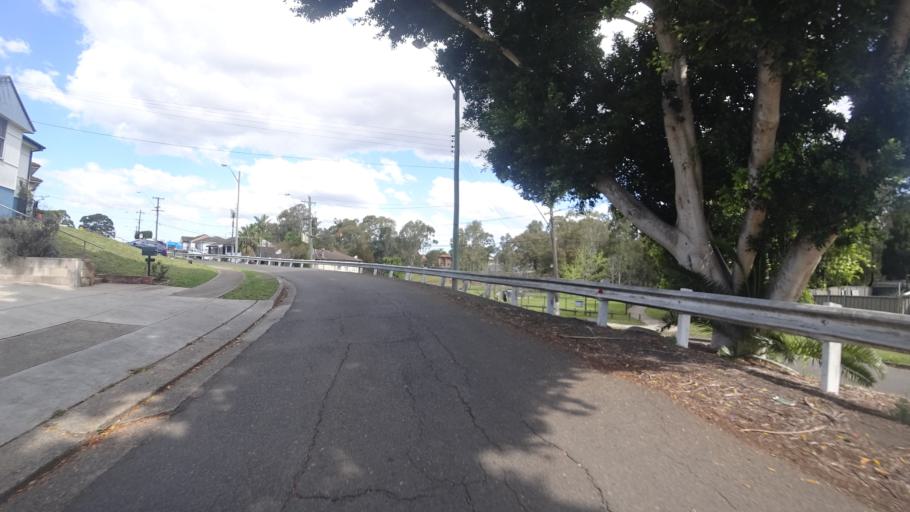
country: AU
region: New South Wales
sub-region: Fairfield
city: Cabramatta West
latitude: -33.9043
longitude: 150.9069
